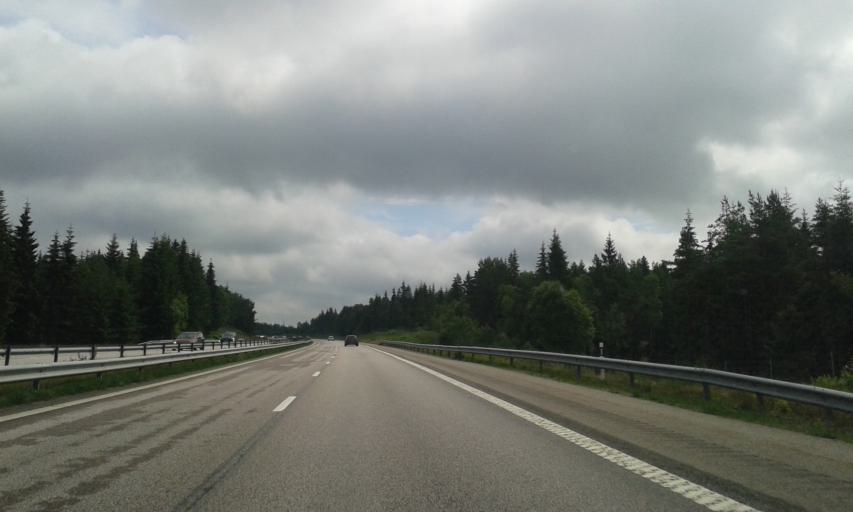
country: SE
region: Vaestra Goetaland
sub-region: Bollebygds Kommun
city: Bollebygd
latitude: 57.6704
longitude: 12.6568
